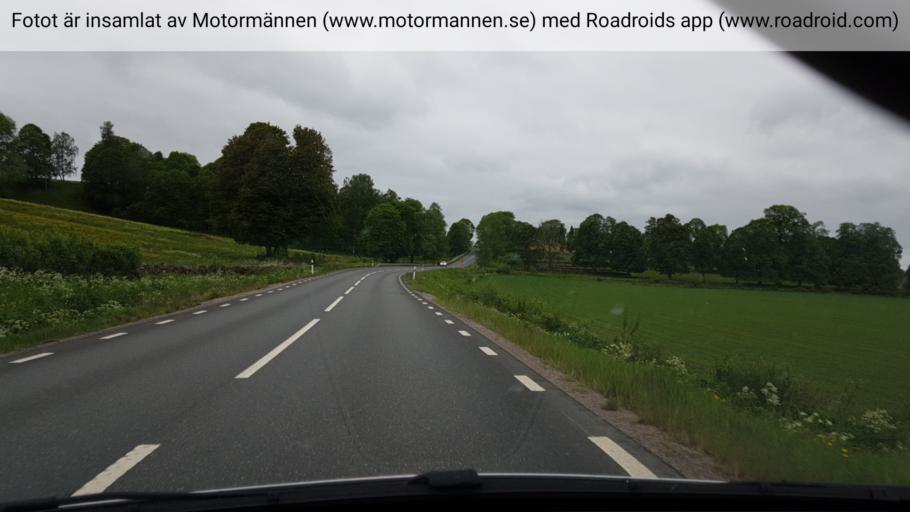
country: SE
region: Joenkoeping
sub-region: Tranas Kommun
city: Tranas
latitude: 57.9955
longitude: 14.9054
